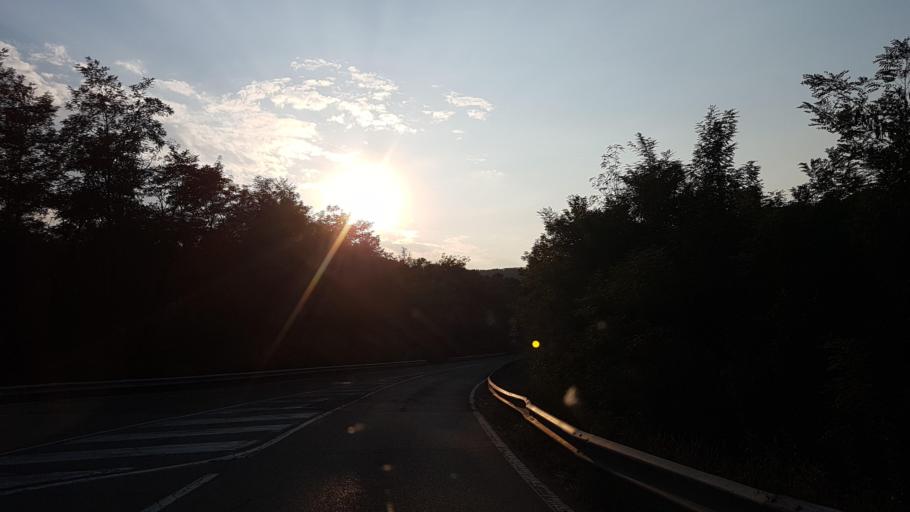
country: IT
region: Emilia-Romagna
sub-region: Provincia di Parma
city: Stazione Valmozzola
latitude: 44.5397
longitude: 9.8951
